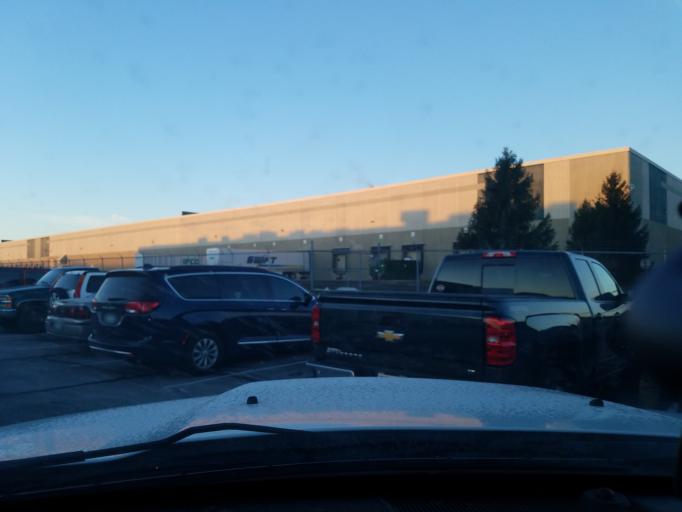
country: US
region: Indiana
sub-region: Boone County
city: Zionsville
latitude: 39.8907
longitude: -86.2559
